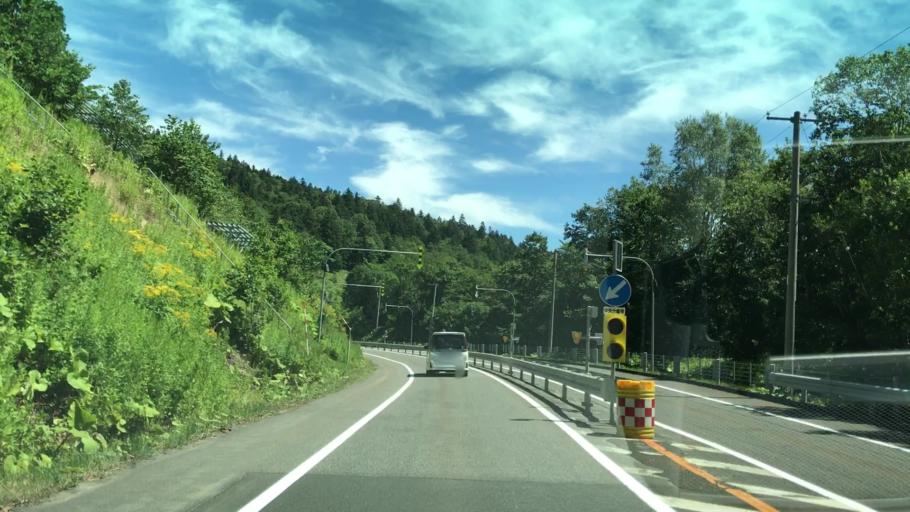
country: JP
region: Hokkaido
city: Shimo-furano
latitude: 42.9642
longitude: 142.6599
